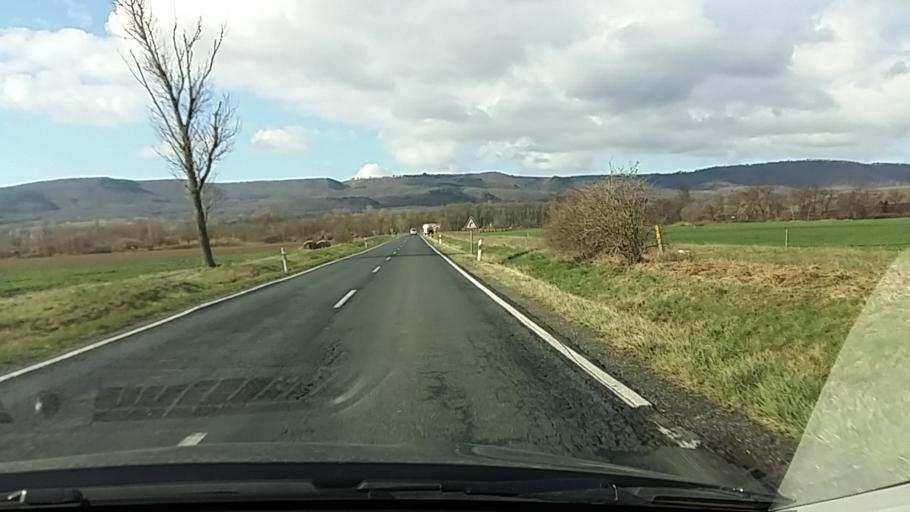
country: HU
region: Veszprem
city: Tapolca
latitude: 46.8471
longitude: 17.3745
